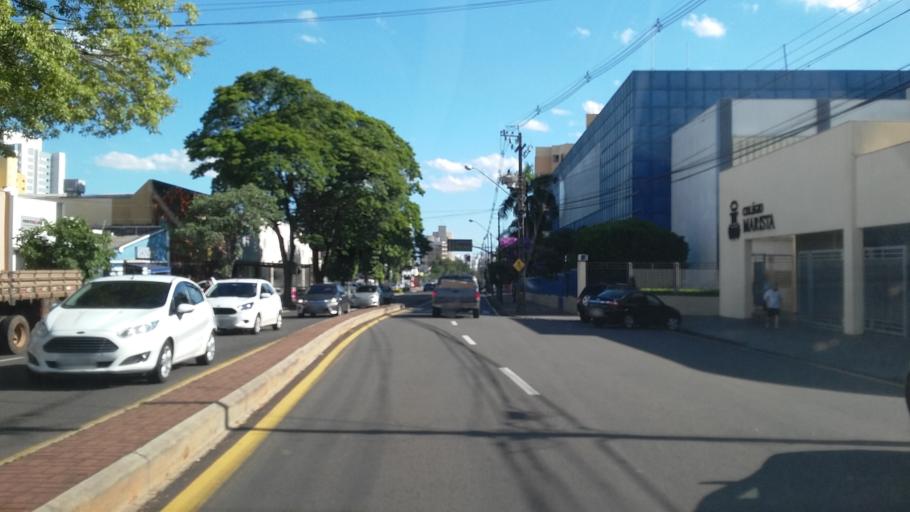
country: BR
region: Parana
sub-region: Londrina
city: Londrina
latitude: -23.3020
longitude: -51.1791
